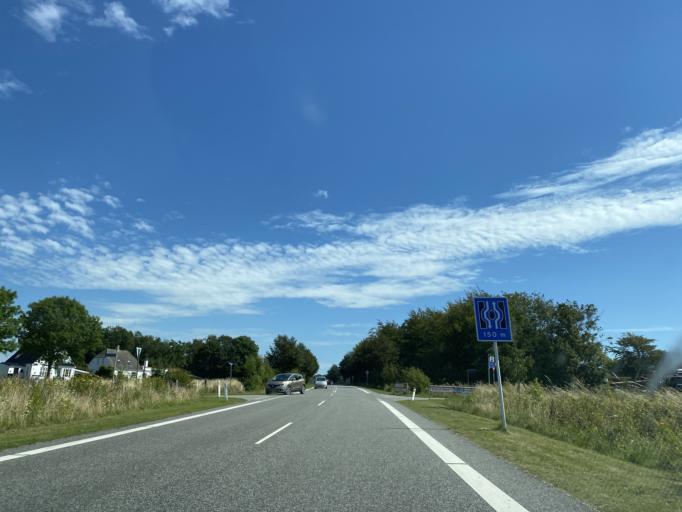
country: DK
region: South Denmark
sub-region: Assens Kommune
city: Harby
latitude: 55.1042
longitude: 10.0973
